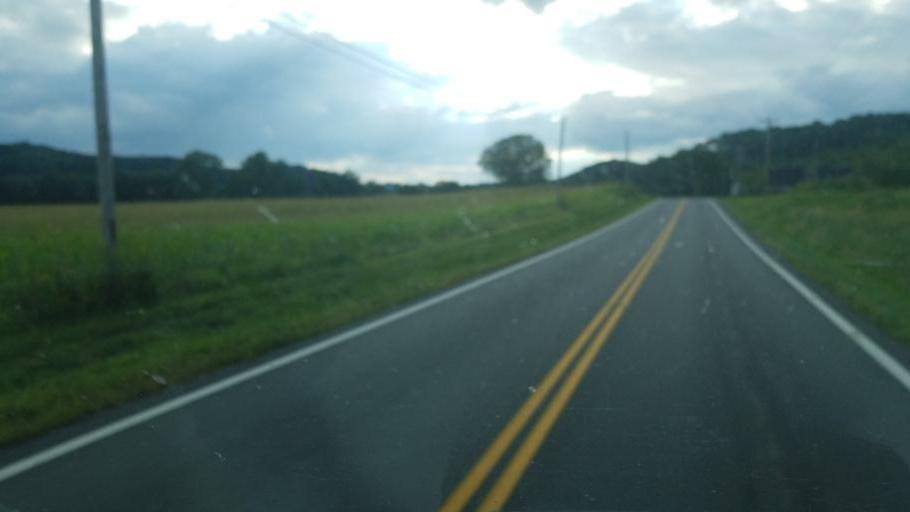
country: US
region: Ohio
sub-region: Holmes County
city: Millersburg
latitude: 40.4822
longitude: -82.0352
